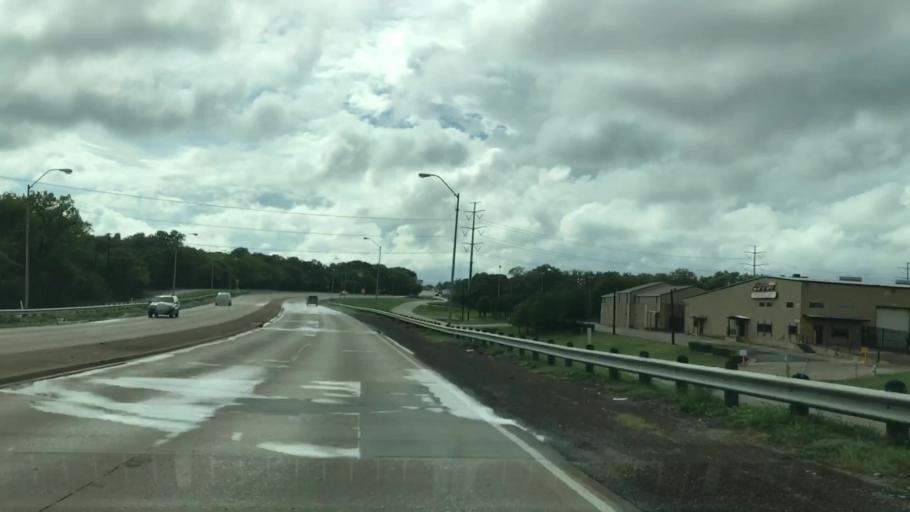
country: US
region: Texas
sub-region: Dallas County
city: Irving
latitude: 32.8094
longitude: -96.9103
